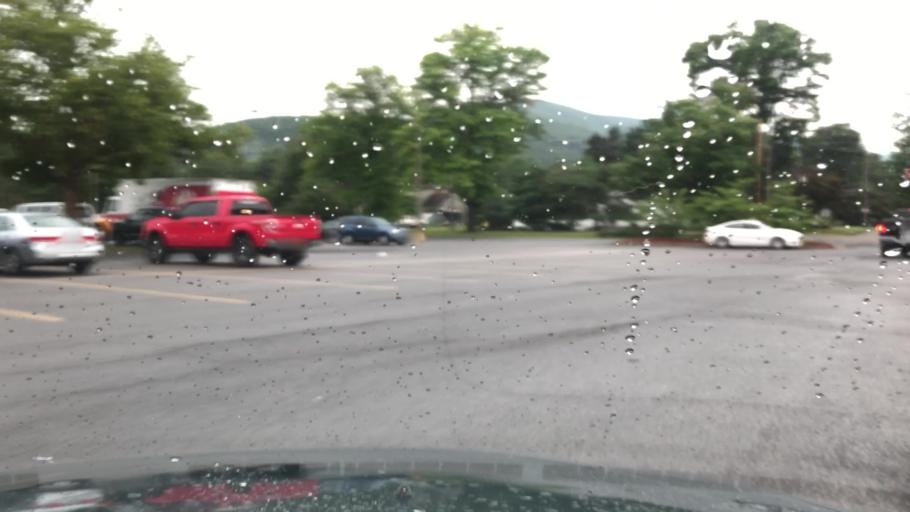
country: US
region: New York
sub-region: Dutchess County
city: Fishkill
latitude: 41.5305
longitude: -73.9069
